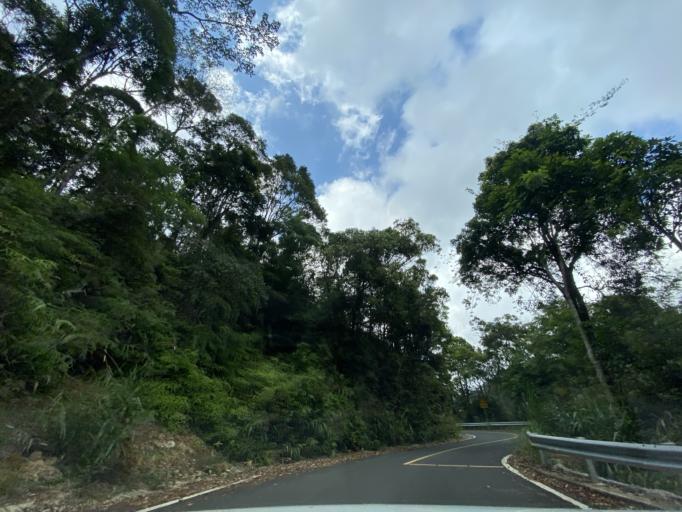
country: CN
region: Hainan
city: Diaoluoshan
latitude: 18.7014
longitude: 109.8829
